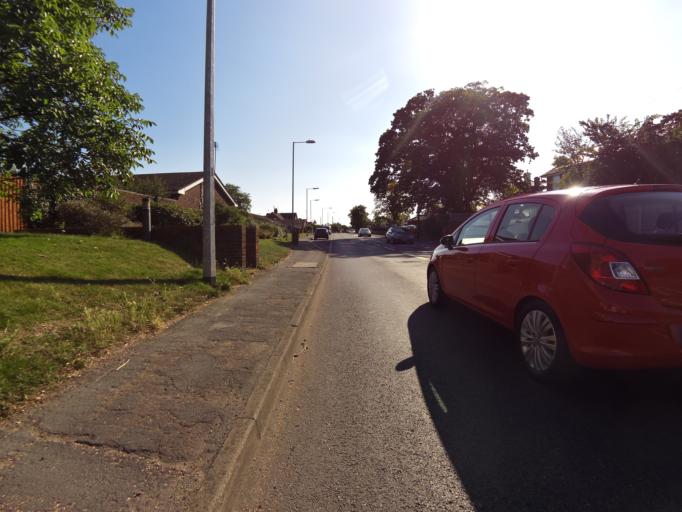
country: GB
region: England
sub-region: Essex
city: Witham
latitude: 51.7952
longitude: 0.6337
